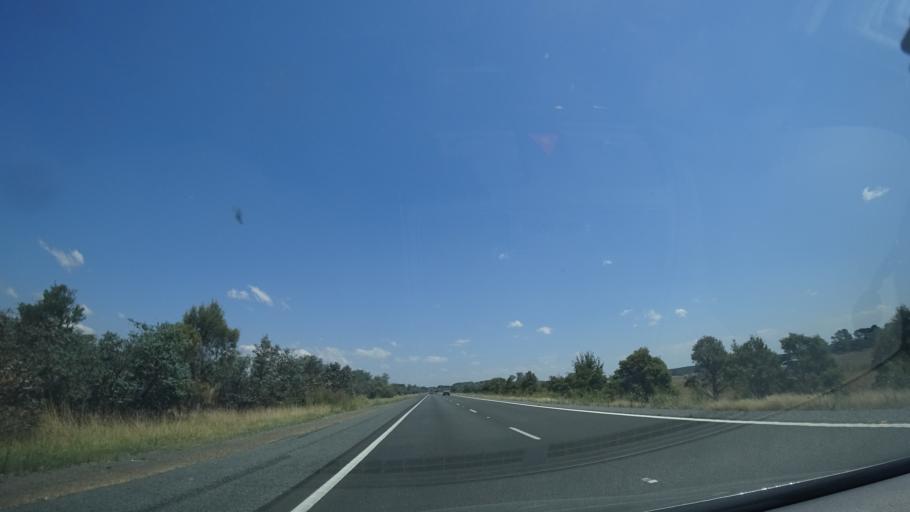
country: AU
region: New South Wales
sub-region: Wingecarribee
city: Moss Vale
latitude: -34.5374
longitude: 150.2807
